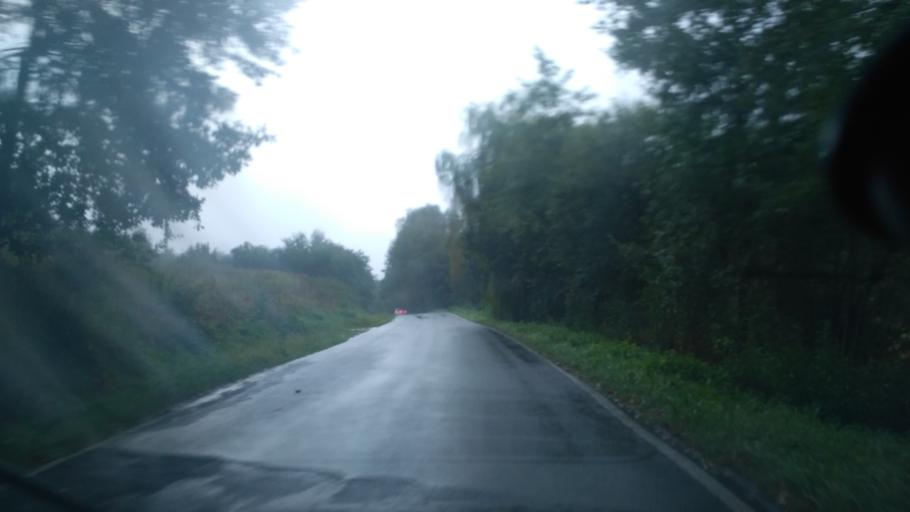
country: PL
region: Subcarpathian Voivodeship
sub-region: Powiat ropczycko-sedziszowski
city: Niedzwiada
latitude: 50.0408
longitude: 21.5442
